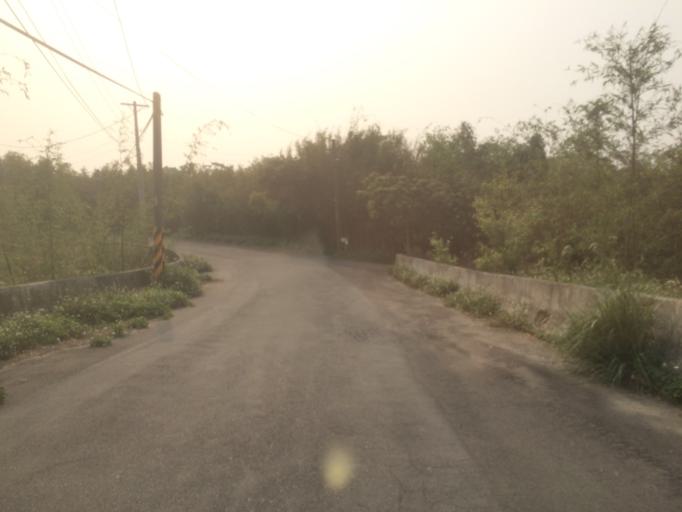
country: TW
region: Taiwan
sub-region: Hsinchu
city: Hsinchu
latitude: 24.7643
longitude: 120.9726
